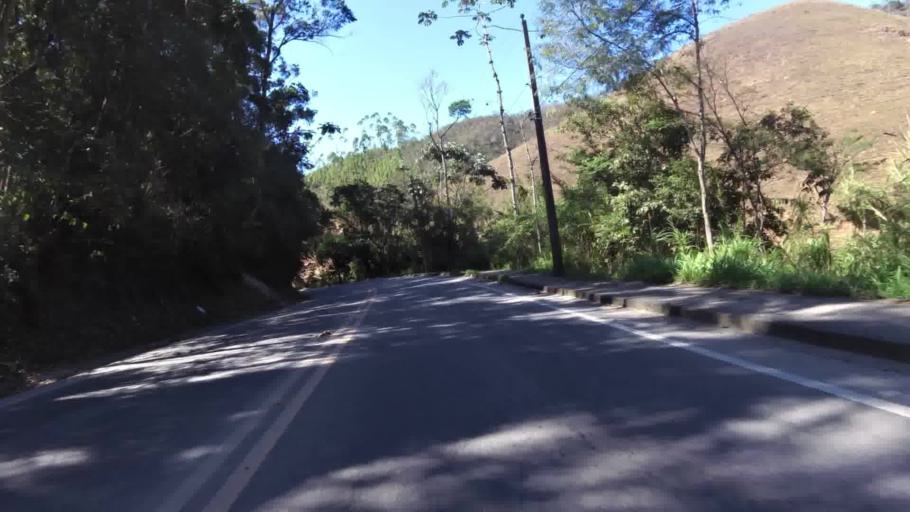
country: BR
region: Espirito Santo
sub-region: Vargem Alta
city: Vargem Alta
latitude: -20.6793
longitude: -41.0210
